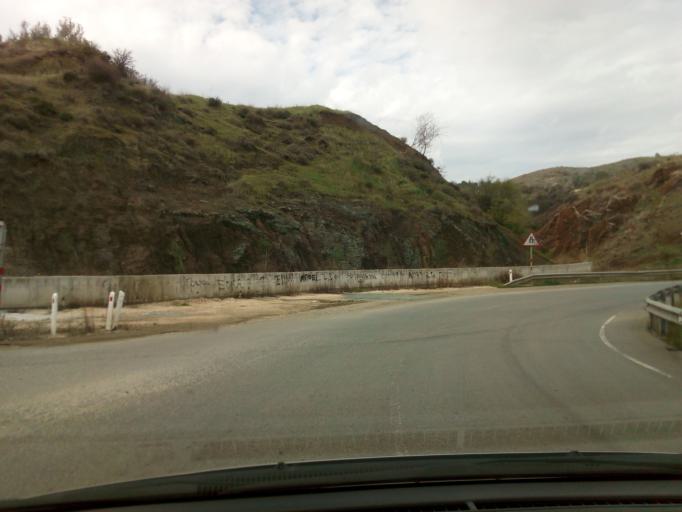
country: CY
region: Lefkosia
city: Klirou
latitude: 35.0115
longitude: 33.1551
